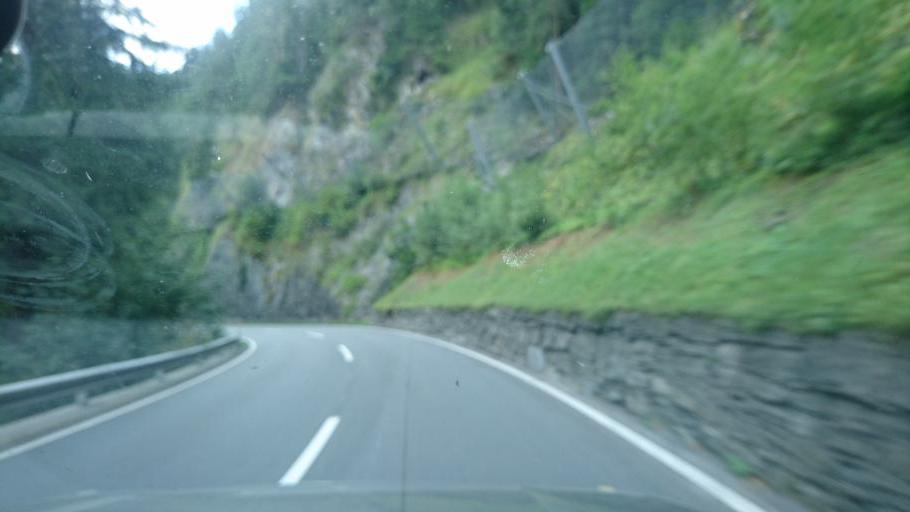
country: AT
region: Tyrol
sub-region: Politischer Bezirk Landeck
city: Pfunds
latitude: 46.9439
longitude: 10.5068
